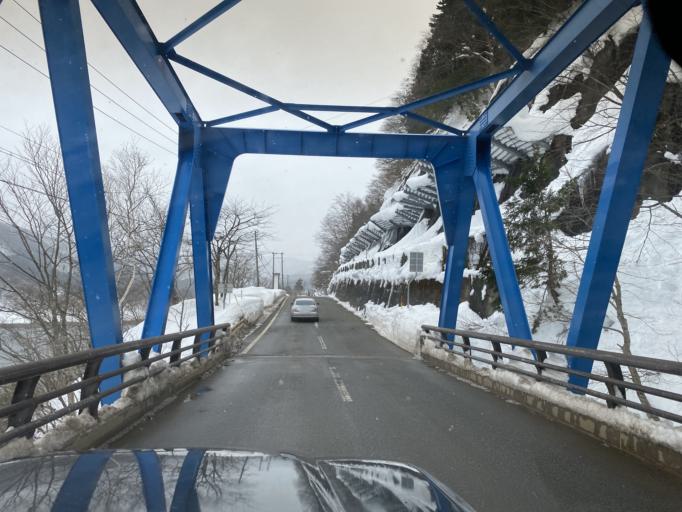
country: JP
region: Gifu
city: Takayama
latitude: 36.0898
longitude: 136.9399
